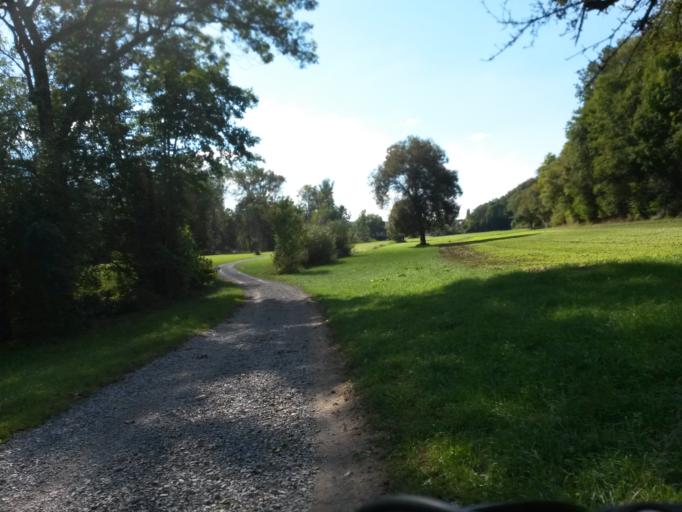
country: DE
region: Baden-Wuerttemberg
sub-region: Regierungsbezirk Stuttgart
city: Oberriexingen
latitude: 48.9350
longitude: 9.0411
